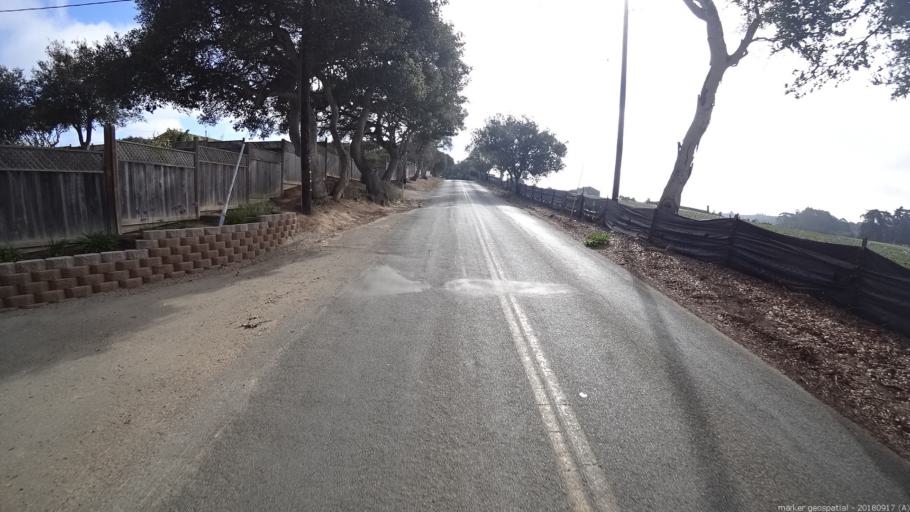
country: US
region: California
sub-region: Monterey County
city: Elkhorn
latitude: 36.7896
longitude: -121.7176
